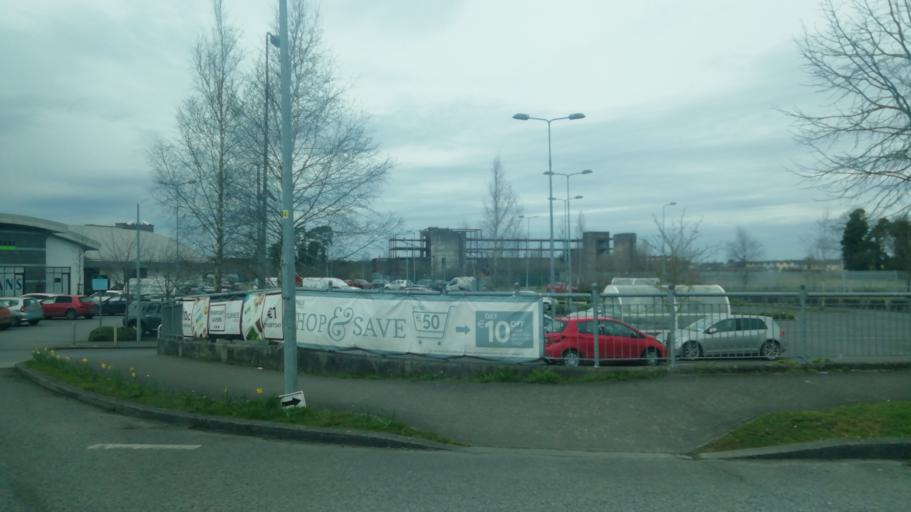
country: IE
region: Leinster
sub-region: Uibh Fhaili
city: Edenderry
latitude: 53.3423
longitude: -7.0572
